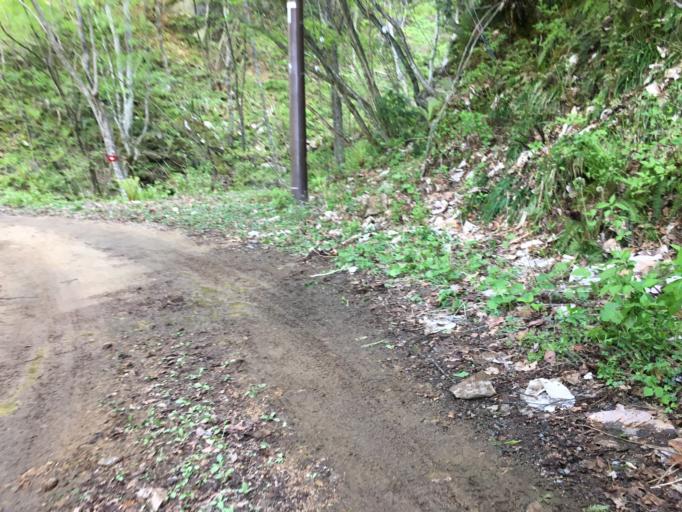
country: JP
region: Nagano
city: Omachi
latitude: 36.5046
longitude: 137.7996
